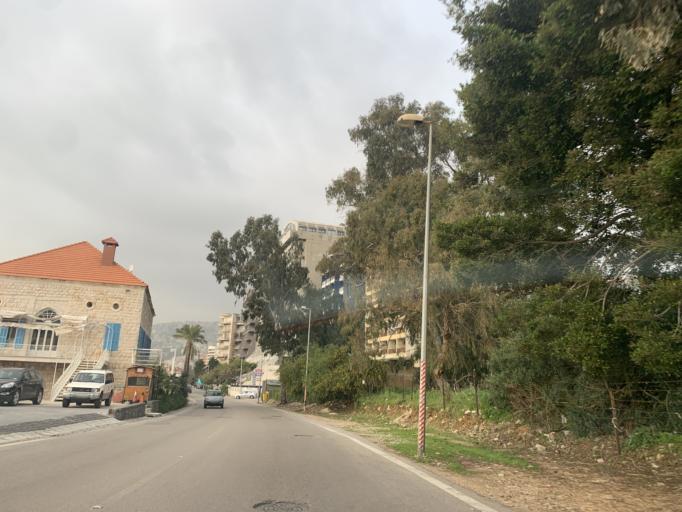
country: LB
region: Mont-Liban
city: Djounie
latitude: 33.9975
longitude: 35.6436
